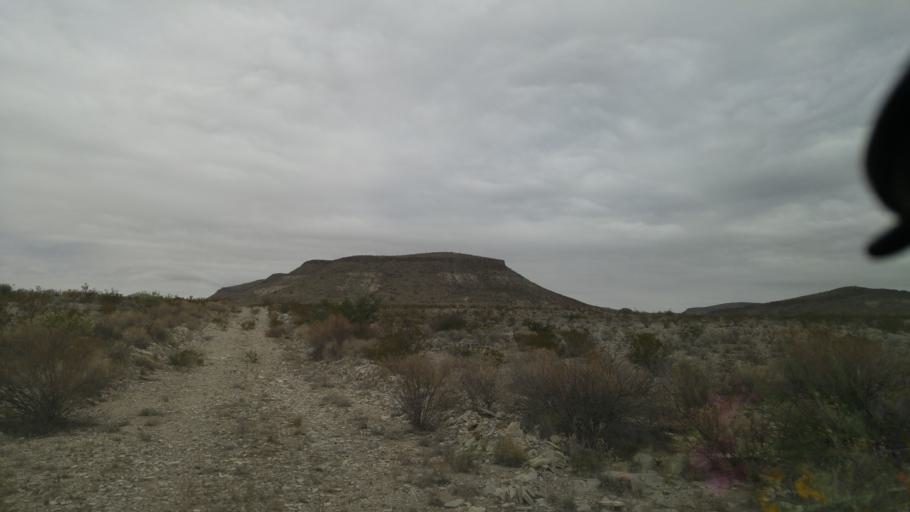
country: US
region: Texas
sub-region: Brewster County
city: Alpine
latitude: 29.5870
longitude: -103.3652
